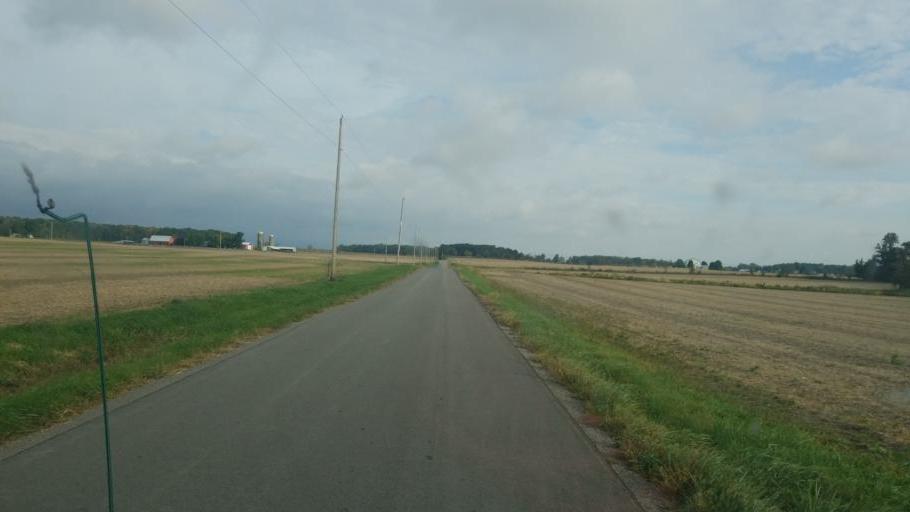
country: US
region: Ohio
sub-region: Wyandot County
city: Carey
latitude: 41.0256
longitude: -83.4487
